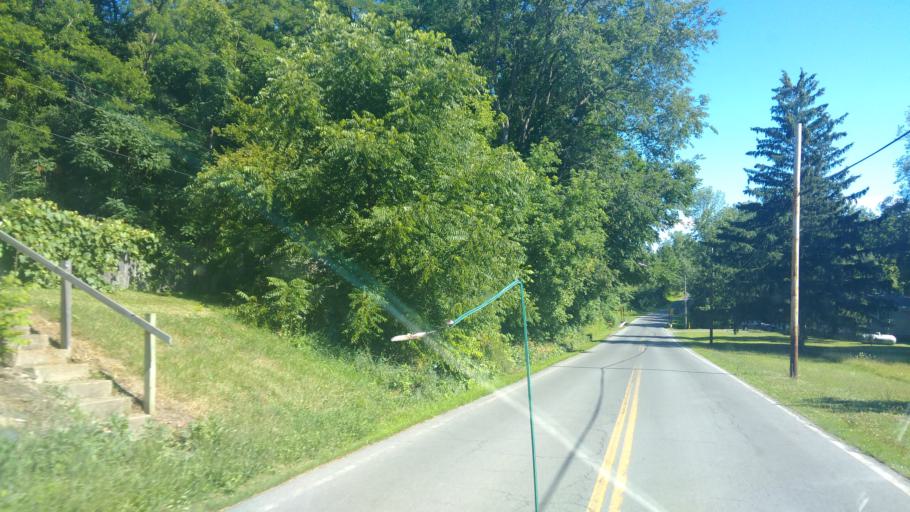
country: US
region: New York
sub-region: Wayne County
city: Clyde
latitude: 43.0103
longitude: -76.8105
